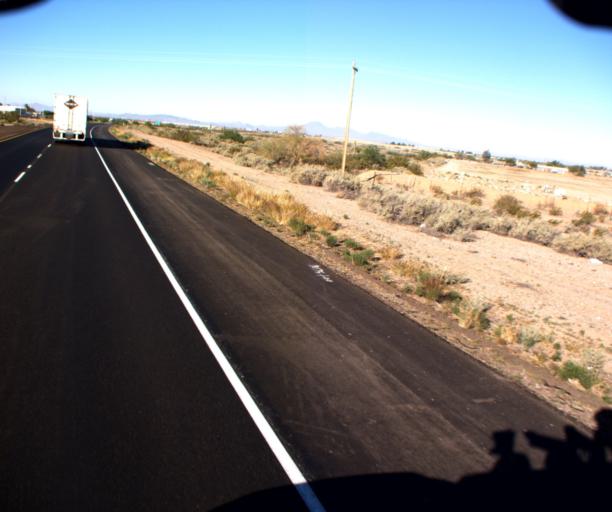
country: US
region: Arizona
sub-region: Pinal County
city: Casa Grande
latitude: 32.8322
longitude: -111.7307
